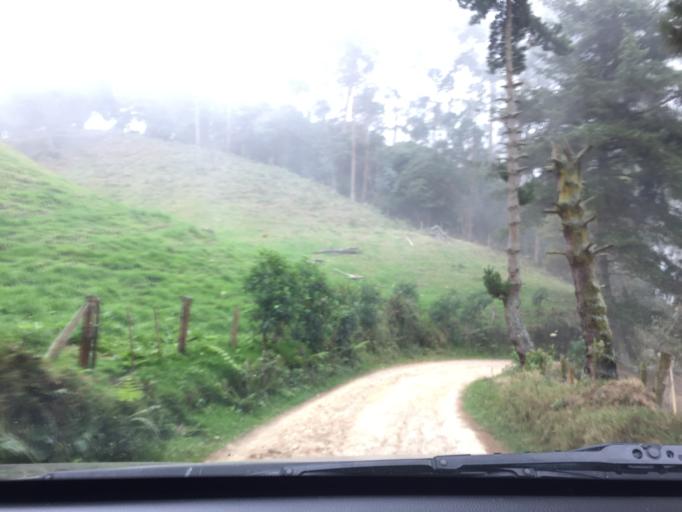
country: CO
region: Cundinamarca
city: Bojaca
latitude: 4.7035
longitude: -74.3625
